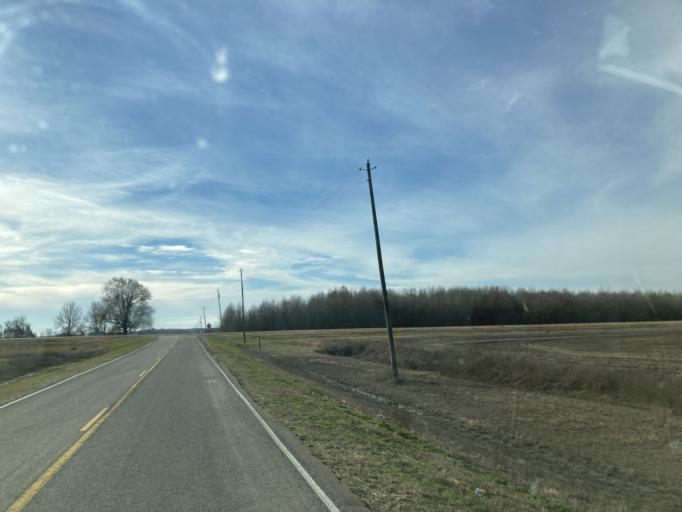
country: US
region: Mississippi
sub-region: Humphreys County
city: Belzoni
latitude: 32.9969
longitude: -90.6226
